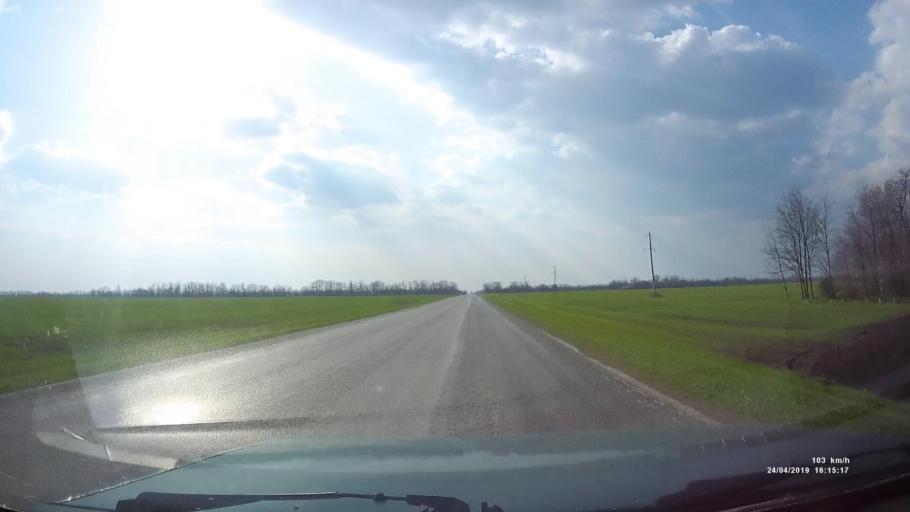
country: RU
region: Rostov
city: Sovetskoye
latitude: 46.7568
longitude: 42.1847
